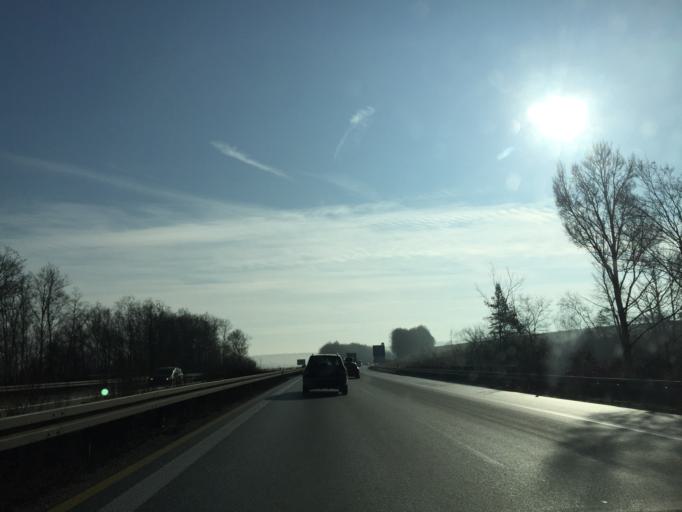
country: DE
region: Bavaria
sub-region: Upper Franconia
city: Schlusselfeld
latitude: 49.7407
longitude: 10.6495
